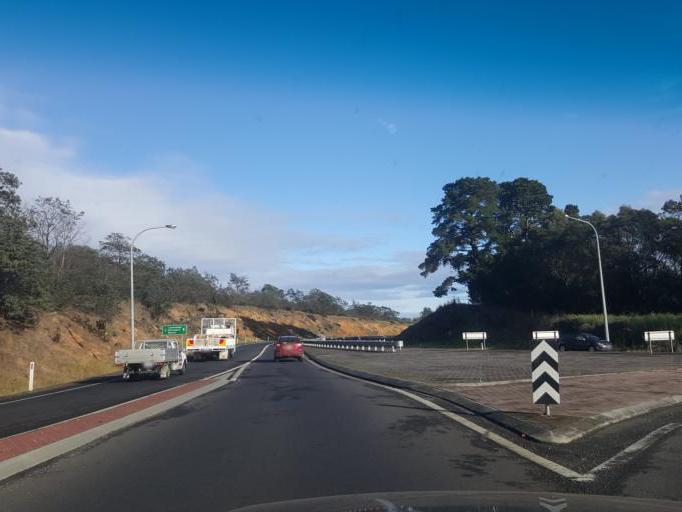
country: AU
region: Tasmania
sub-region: Northern Midlands
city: Perth
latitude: -41.5312
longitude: 147.1865
